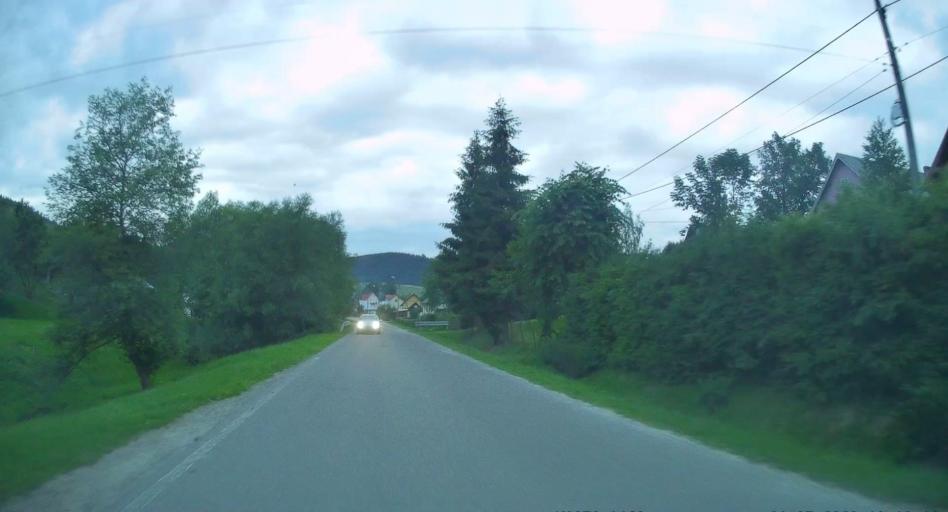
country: PL
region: Lesser Poland Voivodeship
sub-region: Powiat nowosadecki
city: Muszyna
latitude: 49.3826
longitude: 20.9209
